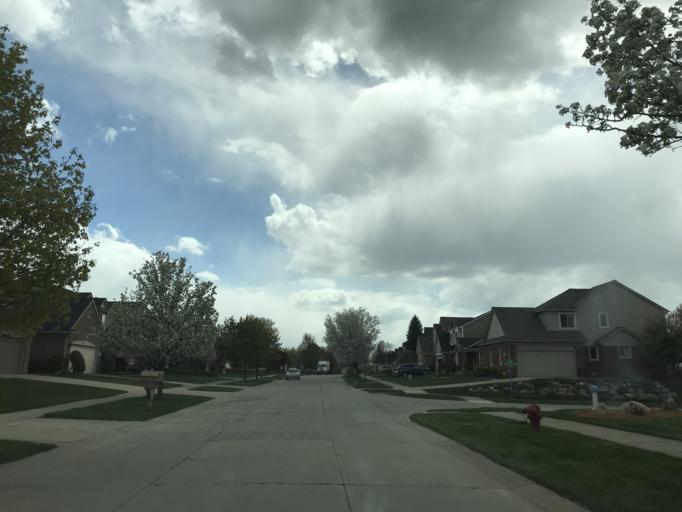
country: US
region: Michigan
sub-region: Wayne County
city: Plymouth
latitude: 42.3726
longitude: -83.5393
